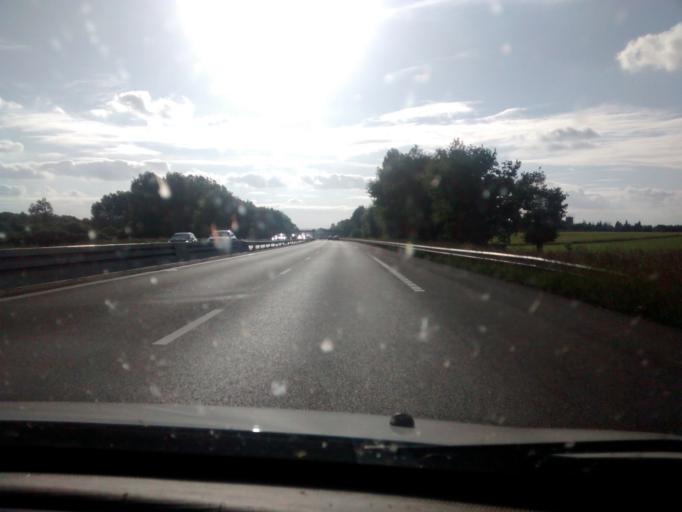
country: FR
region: Brittany
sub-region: Departement d'Ille-et-Vilaine
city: Saint-Didier
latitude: 48.0874
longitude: -1.3549
